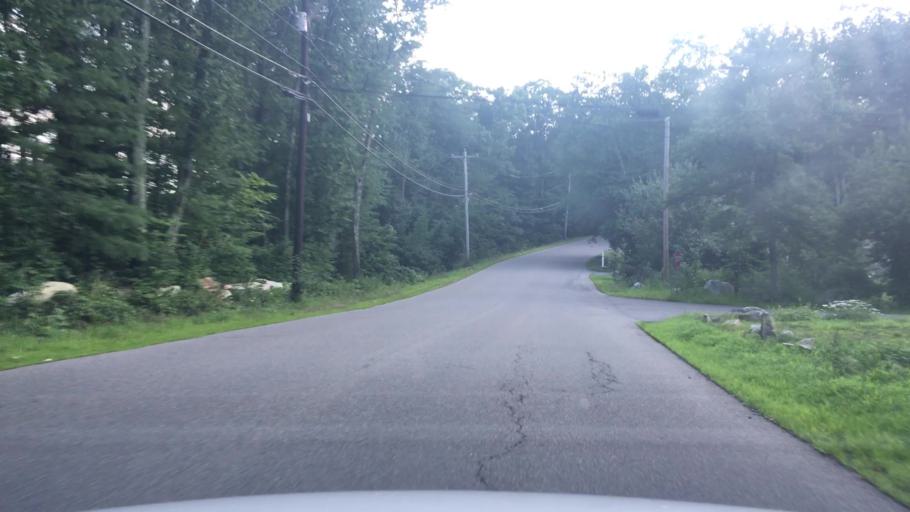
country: US
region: New Hampshire
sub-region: Rockingham County
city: Derry Village
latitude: 42.9220
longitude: -71.3237
